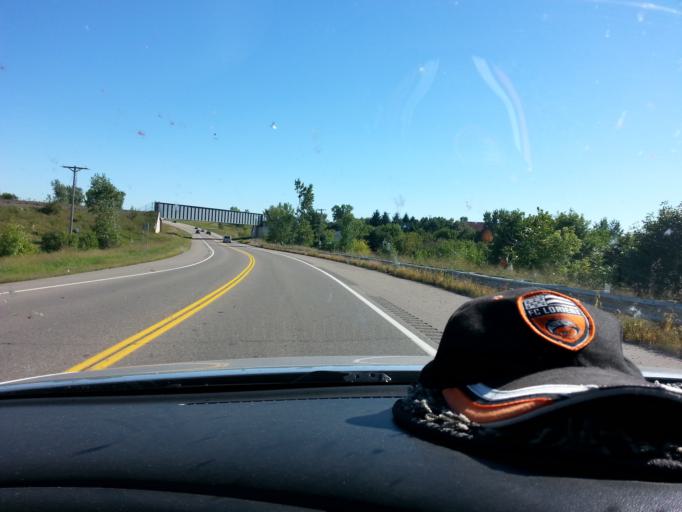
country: US
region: Minnesota
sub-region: Dakota County
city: Rosemount
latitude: 44.7258
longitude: -93.1325
